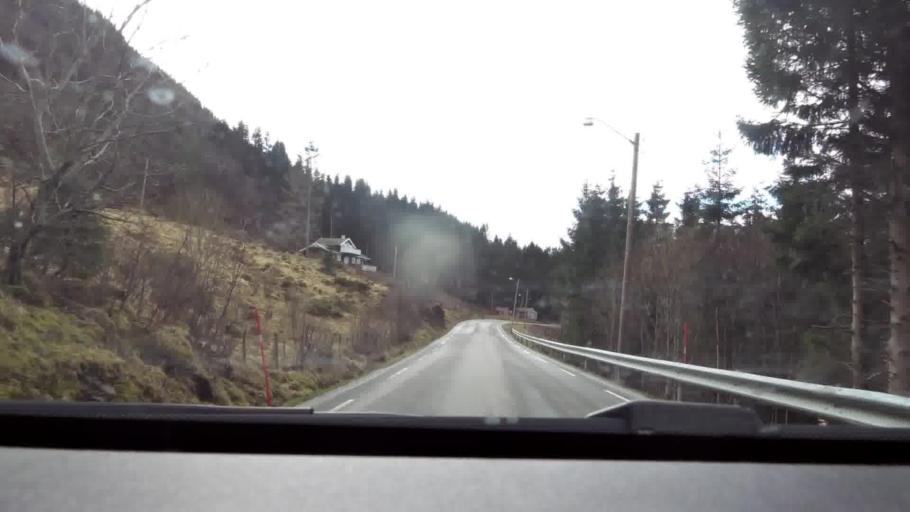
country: NO
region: More og Romsdal
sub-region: Eide
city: Eide
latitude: 62.9177
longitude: 7.5497
